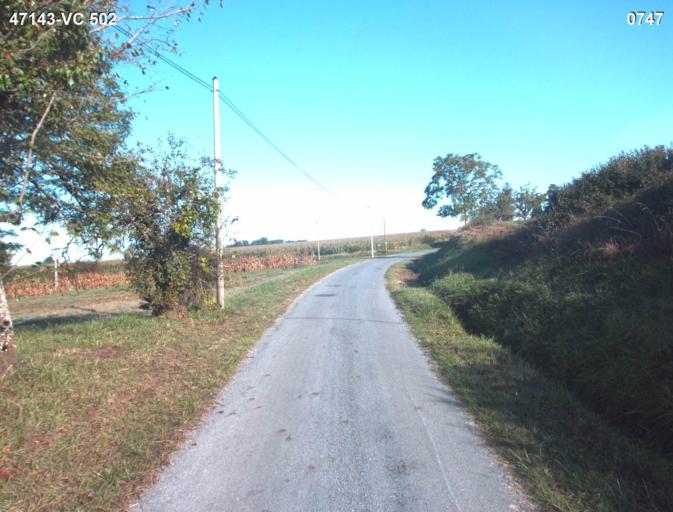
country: FR
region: Aquitaine
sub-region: Departement du Lot-et-Garonne
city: Vianne
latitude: 44.1703
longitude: 0.3268
